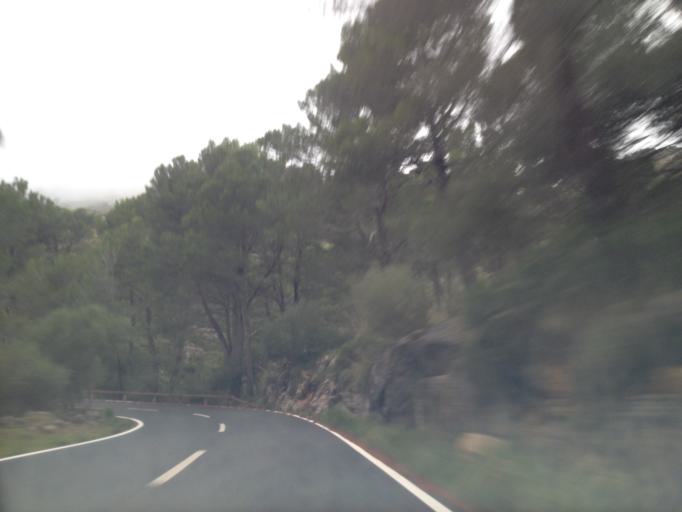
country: ES
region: Balearic Islands
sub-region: Illes Balears
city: Fornalutx
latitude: 39.7948
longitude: 2.7483
